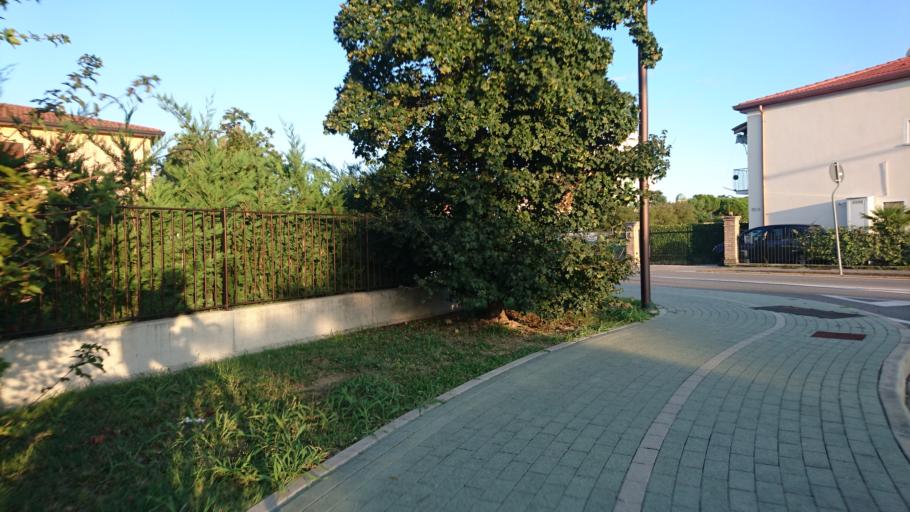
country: IT
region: Veneto
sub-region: Provincia di Padova
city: Montegrotto Terme
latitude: 45.3373
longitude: 11.7803
